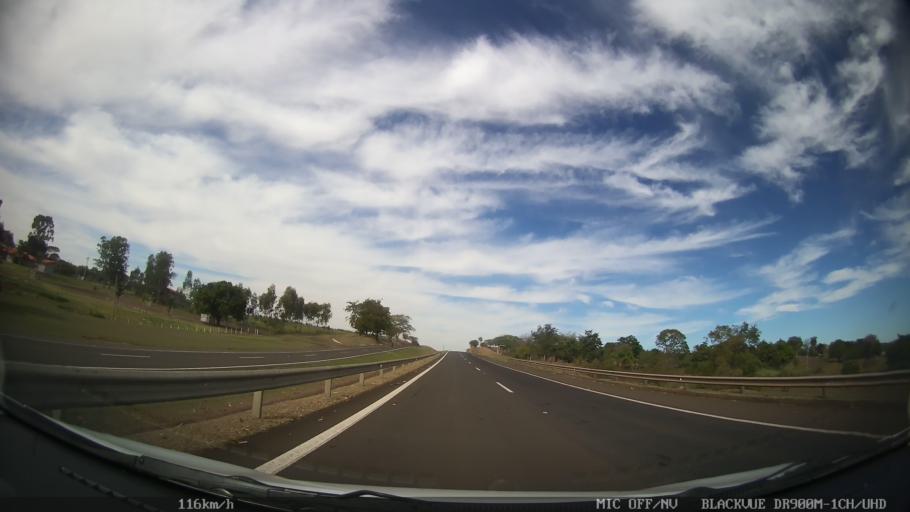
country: BR
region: Sao Paulo
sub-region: Matao
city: Matao
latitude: -21.5747
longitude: -48.4580
